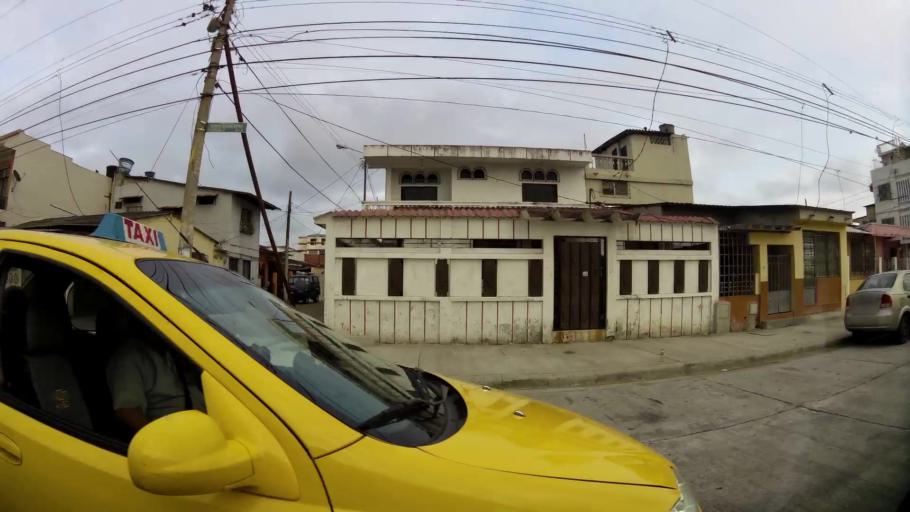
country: EC
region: Guayas
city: Eloy Alfaro
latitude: -2.1722
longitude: -79.8841
